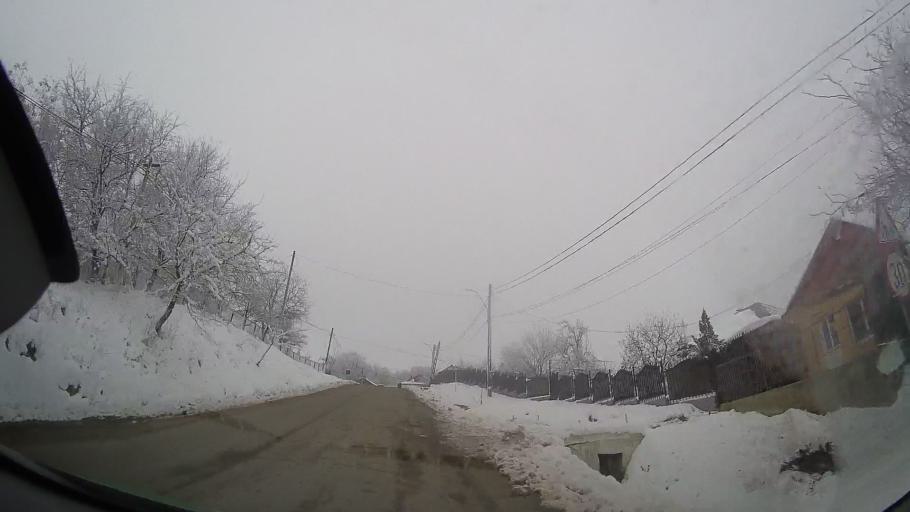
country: RO
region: Iasi
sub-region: Comuna Tibanesti
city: Tibanesti
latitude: 46.8962
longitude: 27.3173
